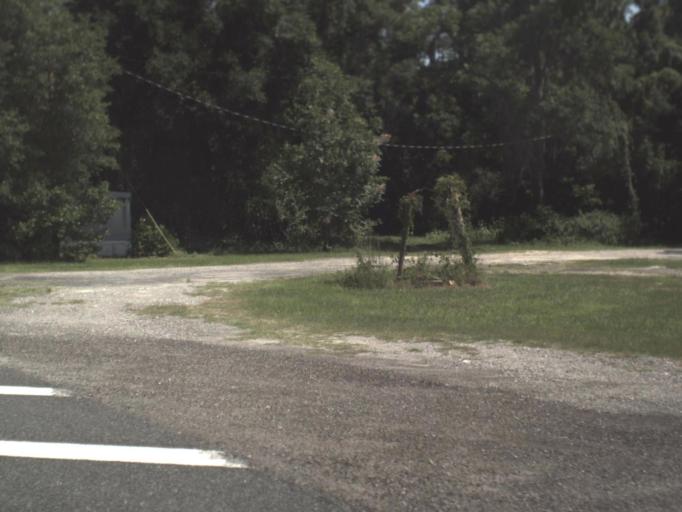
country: US
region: Florida
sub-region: Levy County
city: Chiefland
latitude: 29.4675
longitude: -82.8549
